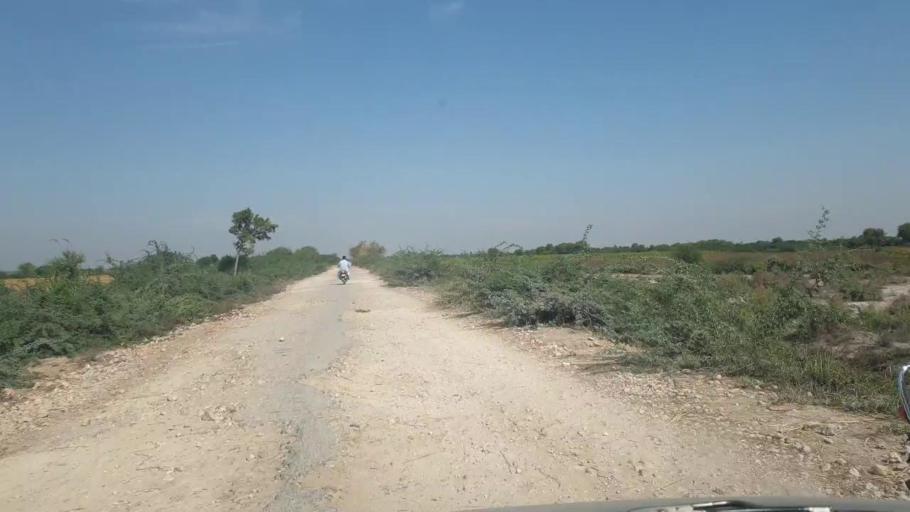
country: PK
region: Sindh
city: Tando Bago
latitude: 24.8640
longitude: 68.9973
